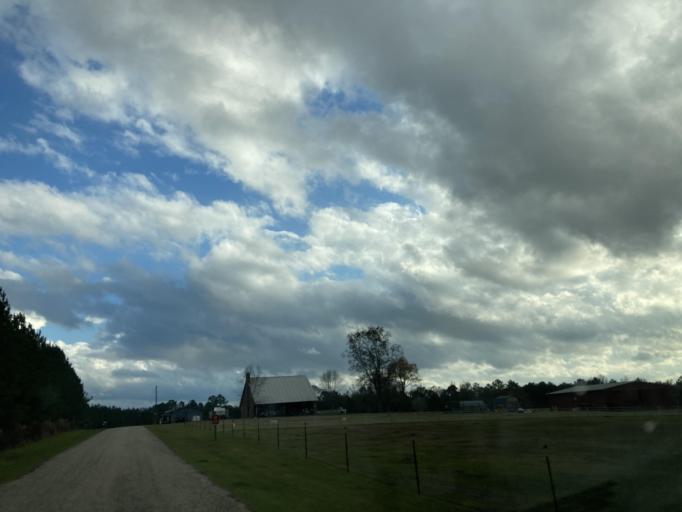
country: US
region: Mississippi
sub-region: Marion County
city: Columbia
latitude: 31.1786
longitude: -89.6648
